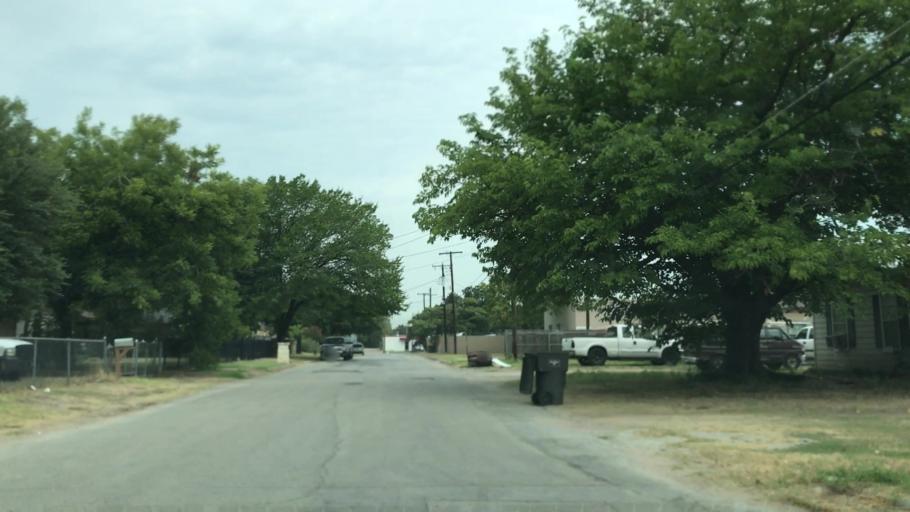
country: US
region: Texas
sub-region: Tarrant County
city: Haltom City
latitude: 32.7671
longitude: -97.2857
